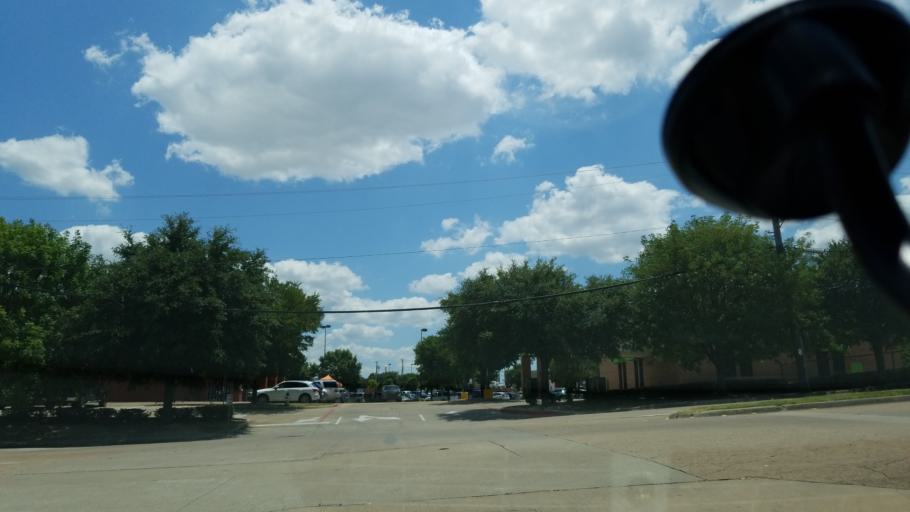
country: US
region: Texas
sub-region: Dallas County
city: Cockrell Hill
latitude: 32.6937
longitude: -96.8563
